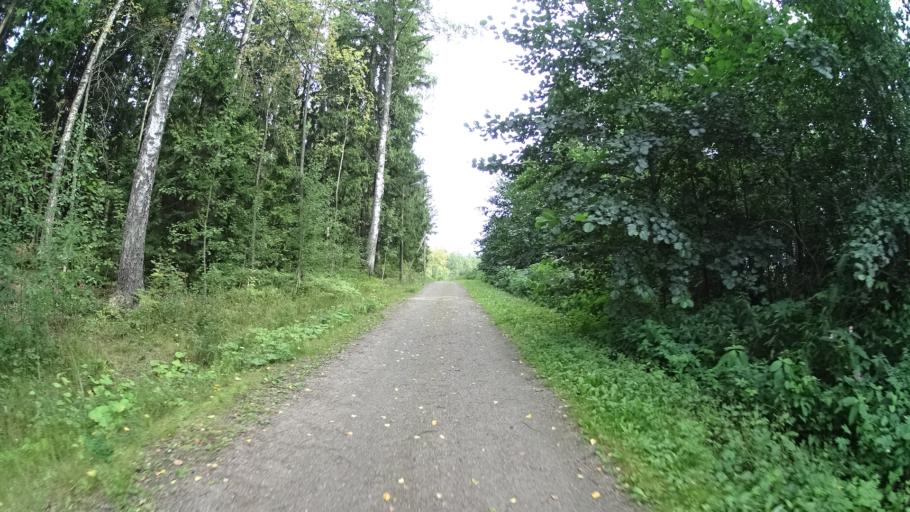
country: FI
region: Uusimaa
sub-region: Helsinki
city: Kilo
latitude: 60.2046
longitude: 24.7832
